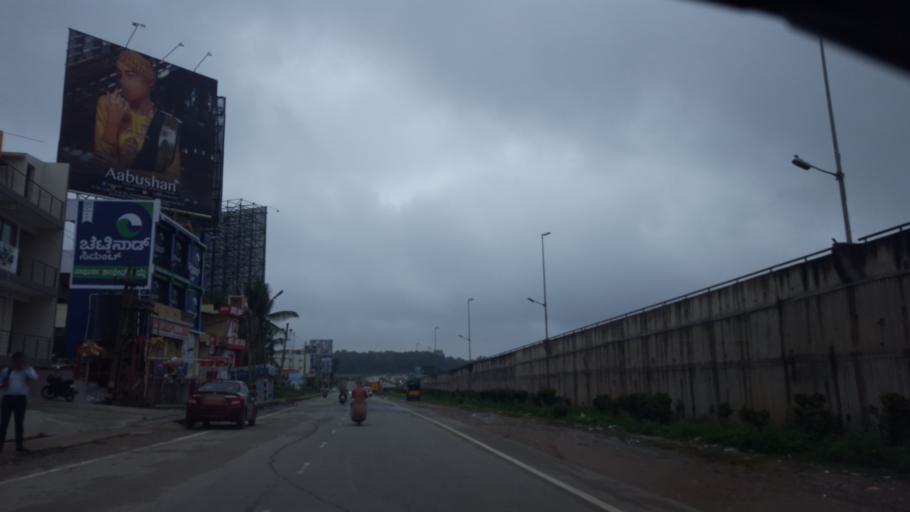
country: IN
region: Karnataka
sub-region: Bangalore Urban
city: Yelahanka
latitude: 13.1429
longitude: 77.6177
